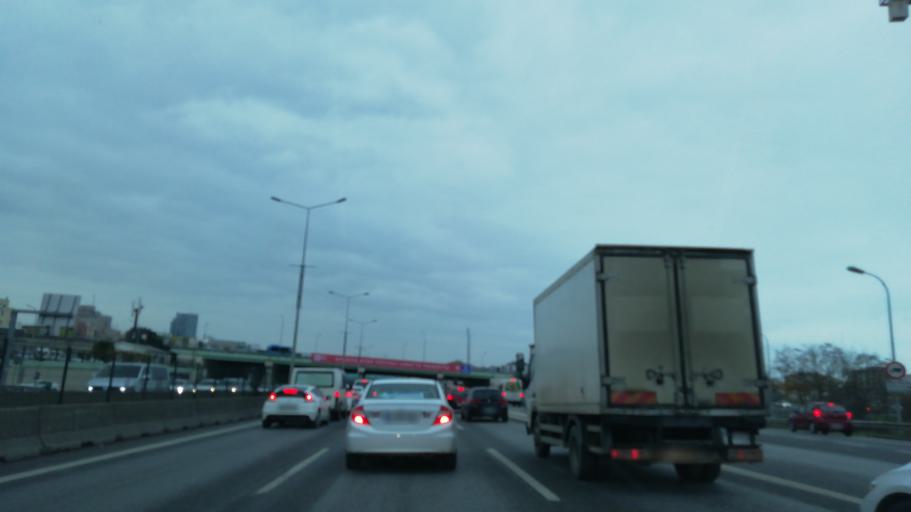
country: TR
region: Istanbul
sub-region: Atasehir
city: Atasehir
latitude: 40.9661
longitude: 29.1042
